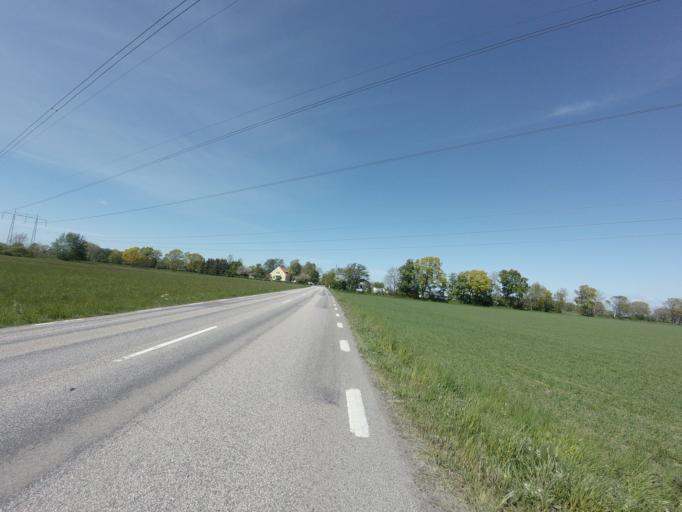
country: SE
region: Skane
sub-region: Helsingborg
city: Odakra
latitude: 56.1362
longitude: 12.6901
